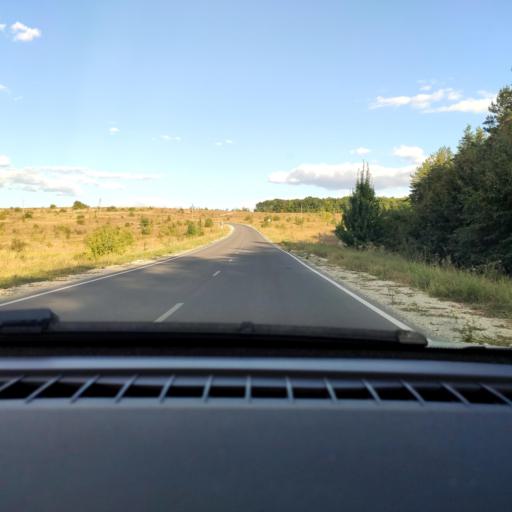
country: RU
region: Voronezj
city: Semiluki
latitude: 51.6570
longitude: 38.9959
